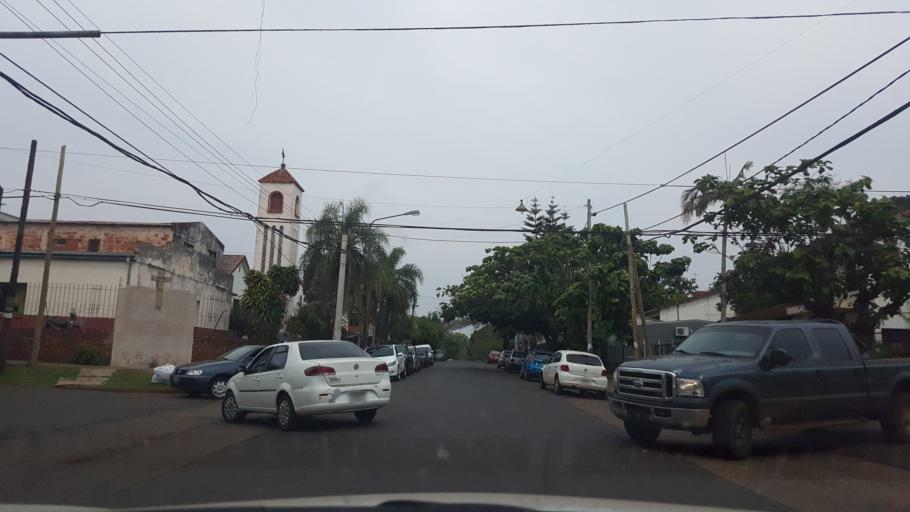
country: AR
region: Misiones
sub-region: Departamento de Capital
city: Posadas
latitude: -27.3744
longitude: -55.9118
